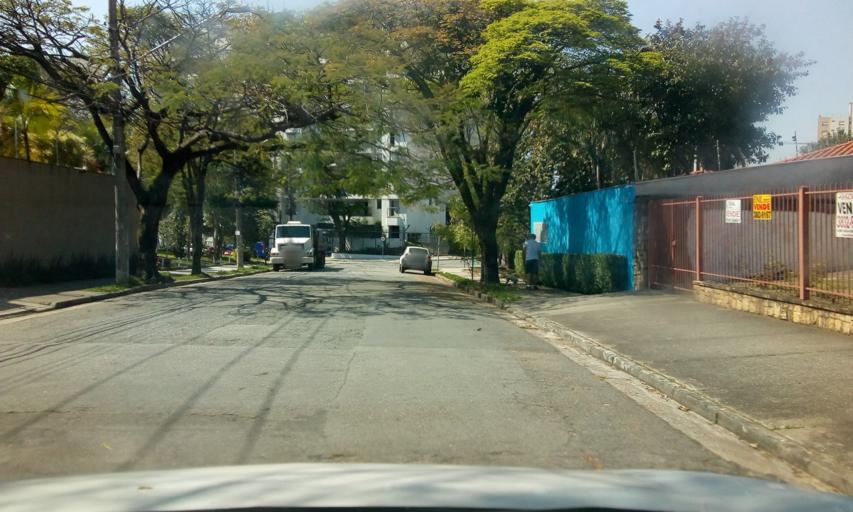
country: BR
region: Sao Paulo
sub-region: Sao Paulo
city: Sao Paulo
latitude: -23.5231
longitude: -46.7119
